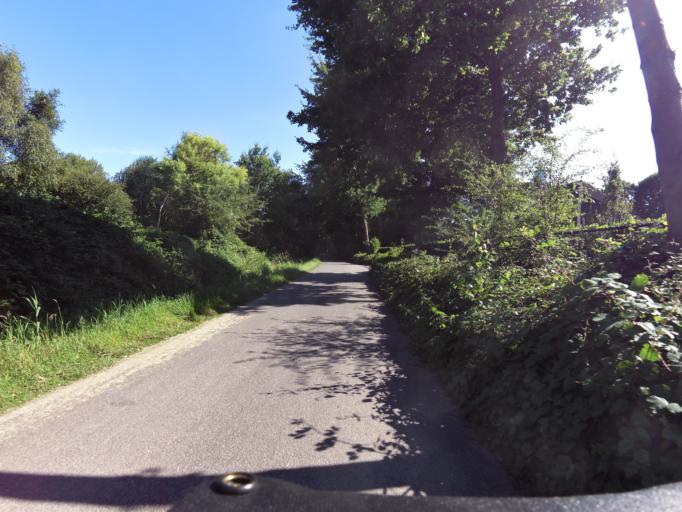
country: NL
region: Zeeland
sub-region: Schouwen-Duiveland
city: Haamstede
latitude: 51.7091
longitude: 3.7351
